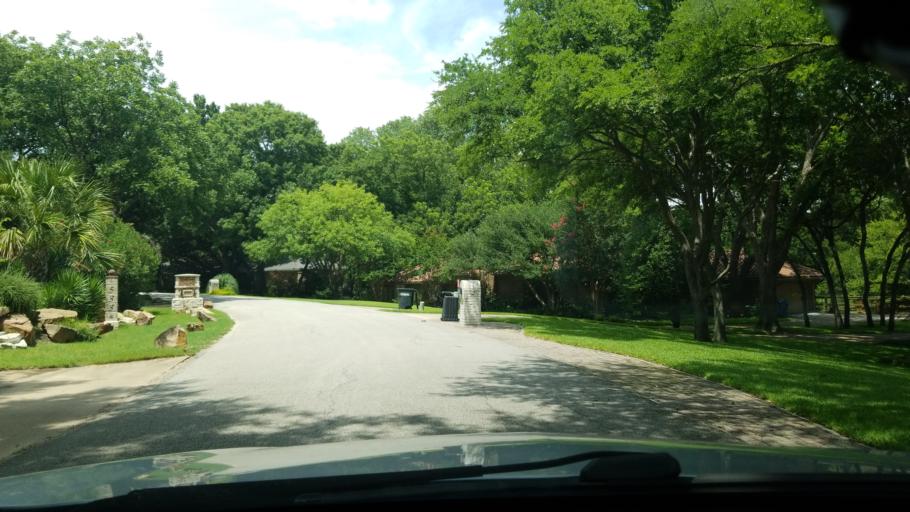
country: US
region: Texas
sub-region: Dallas County
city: Coppell
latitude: 32.9577
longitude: -96.9835
